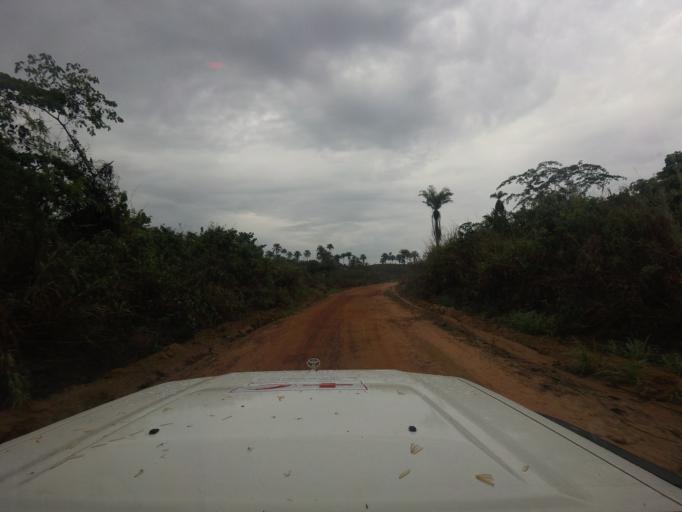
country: LR
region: Lofa
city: Voinjama
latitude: 8.4068
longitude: -9.7789
